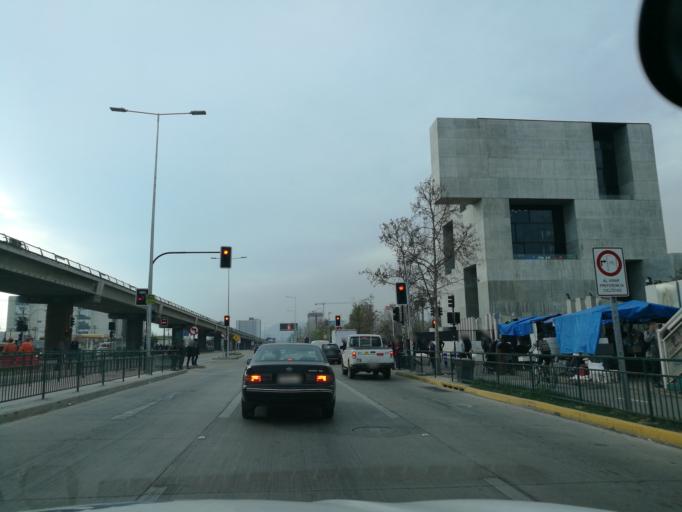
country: CL
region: Santiago Metropolitan
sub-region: Provincia de Santiago
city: Villa Presidente Frei, Nunoa, Santiago, Chile
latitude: -33.4989
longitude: -70.6156
